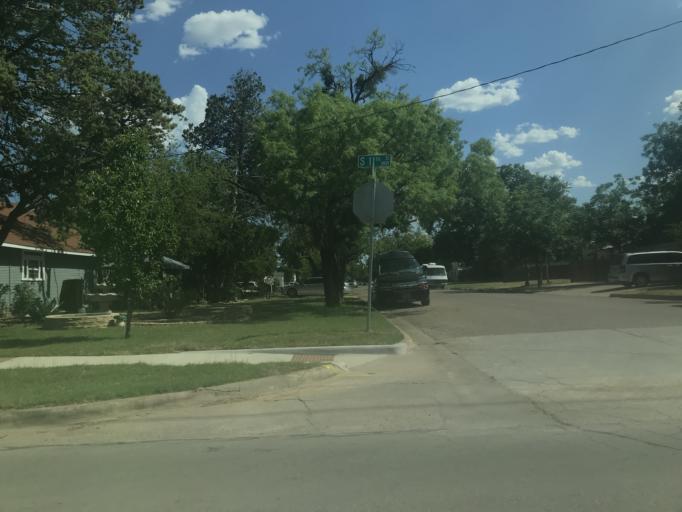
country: US
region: Texas
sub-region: Taylor County
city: Abilene
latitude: 32.4374
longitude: -99.7523
